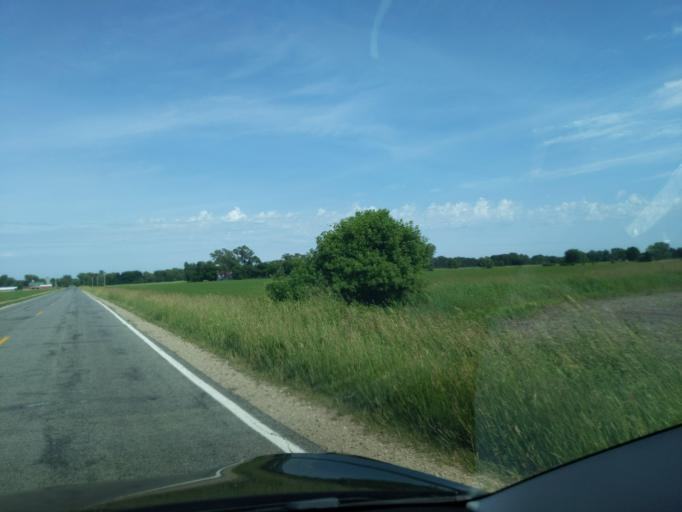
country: US
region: Michigan
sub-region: Newaygo County
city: Fremont
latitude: 43.4239
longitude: -86.0045
